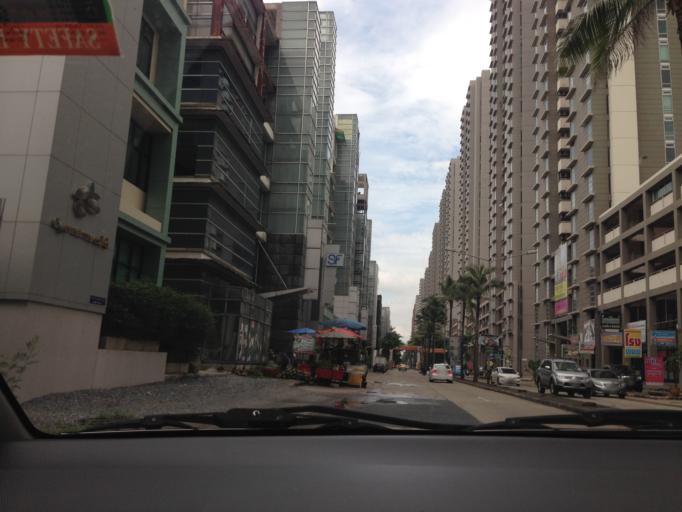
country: TH
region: Nonthaburi
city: Pak Kret
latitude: 13.9212
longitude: 100.5385
